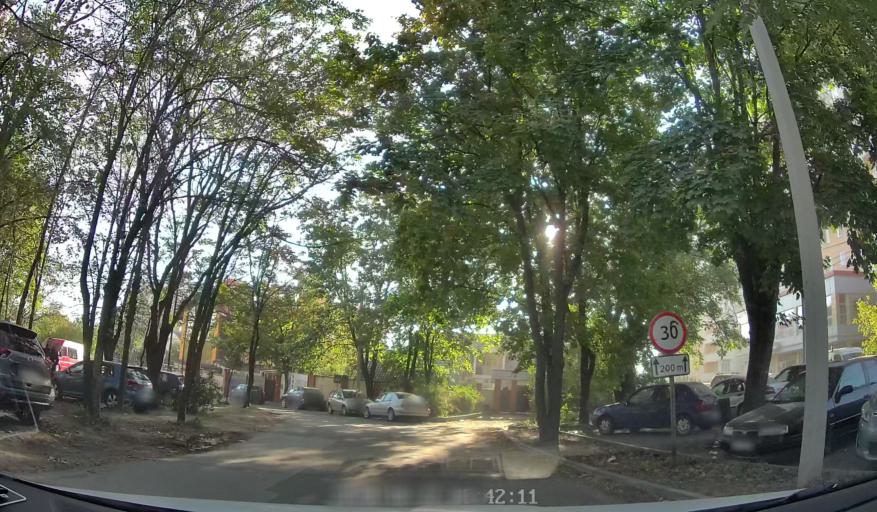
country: MD
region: Chisinau
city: Chisinau
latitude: 46.9981
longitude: 28.8356
